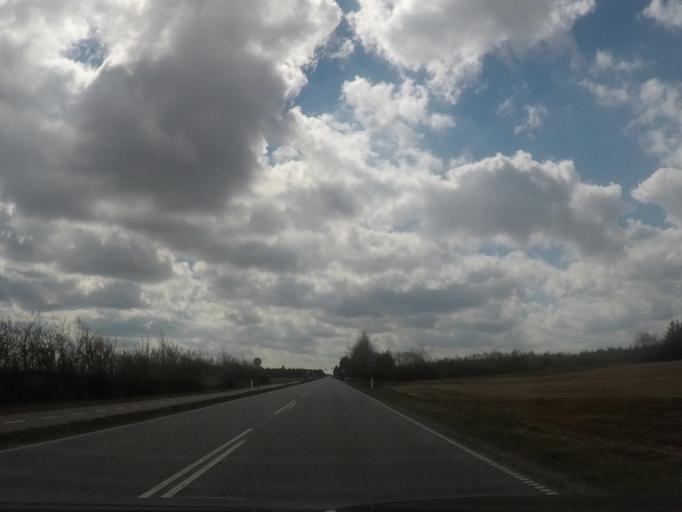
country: DK
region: South Denmark
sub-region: Kolding Kommune
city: Kolding
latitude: 55.5518
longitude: 9.4902
